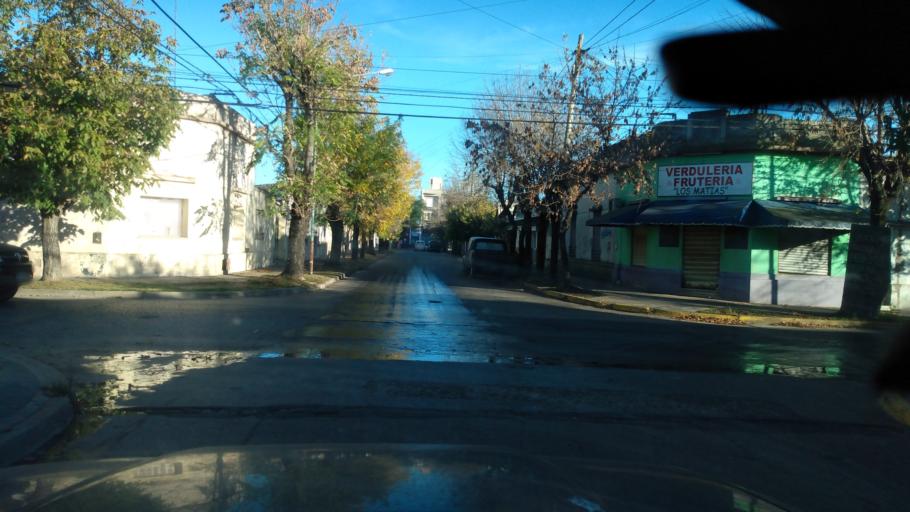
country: AR
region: Buenos Aires
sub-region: Partido de Lujan
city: Lujan
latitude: -34.5629
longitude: -59.1104
